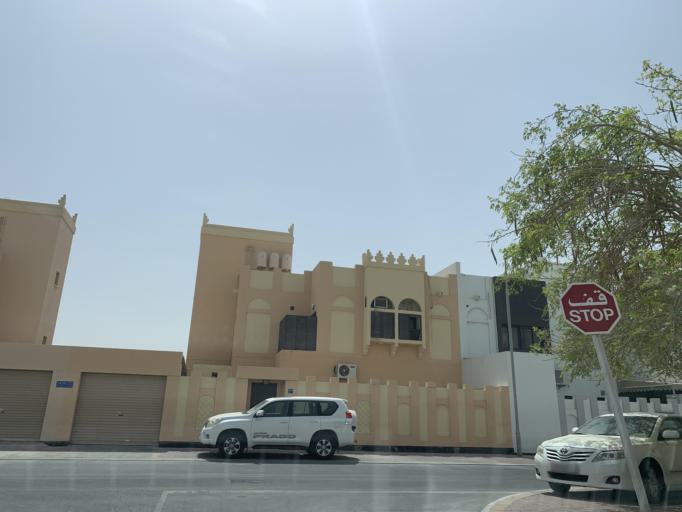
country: BH
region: Northern
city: Madinat `Isa
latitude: 26.1699
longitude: 50.5215
